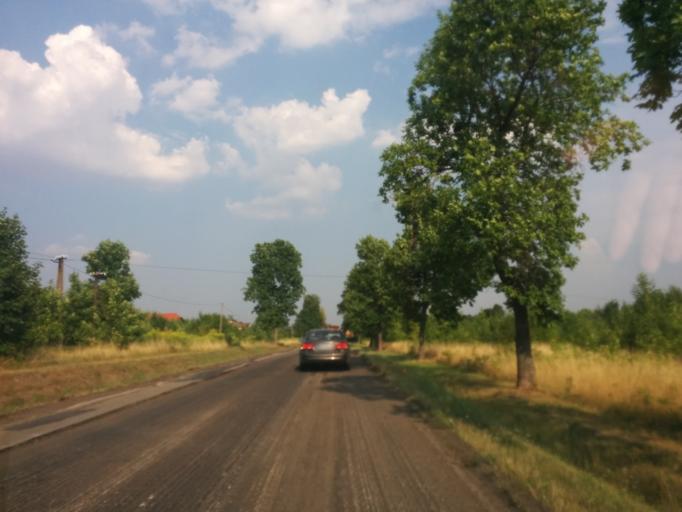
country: PL
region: Silesian Voivodeship
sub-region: Powiat zawiercianski
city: Wlodowice
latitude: 50.5964
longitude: 19.4459
